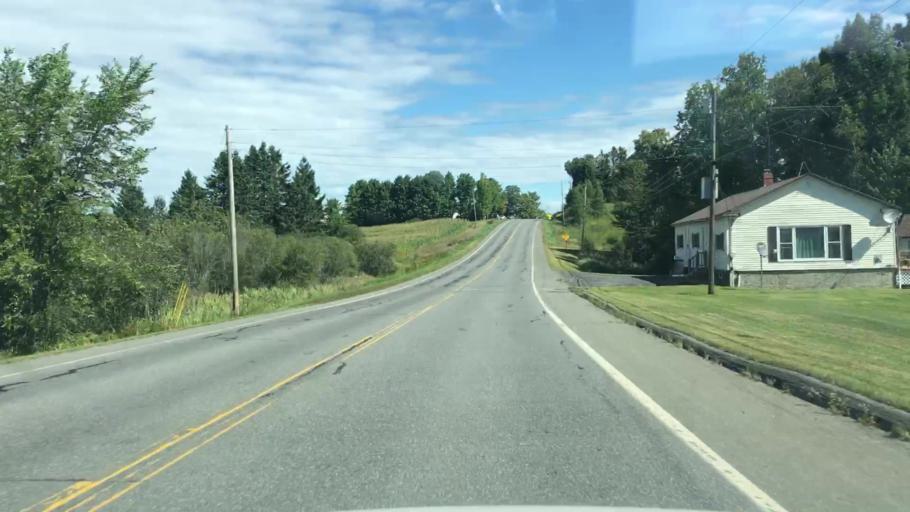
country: US
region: Maine
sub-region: Penobscot County
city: Dexter
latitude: 45.0725
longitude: -69.2362
